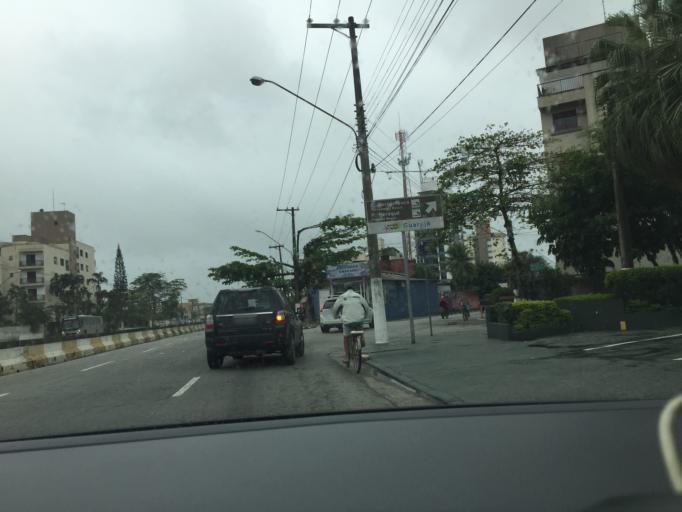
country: BR
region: Sao Paulo
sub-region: Guaruja
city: Guaruja
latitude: -23.9801
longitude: -46.2258
